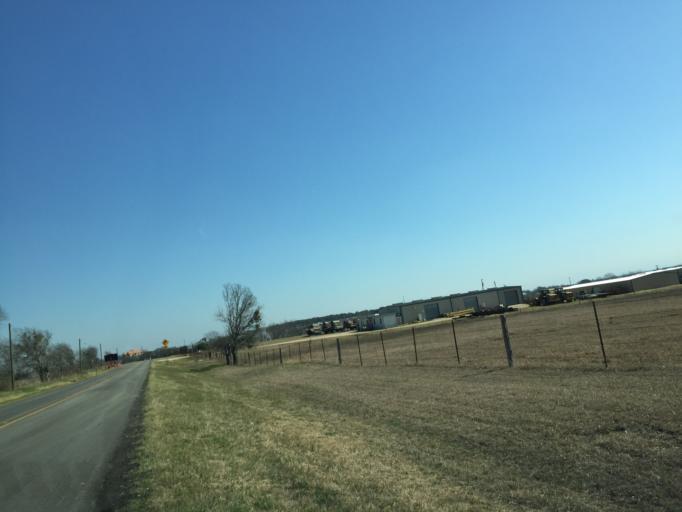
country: US
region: Texas
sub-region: Williamson County
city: Serenada
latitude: 30.7364
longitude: -97.6017
